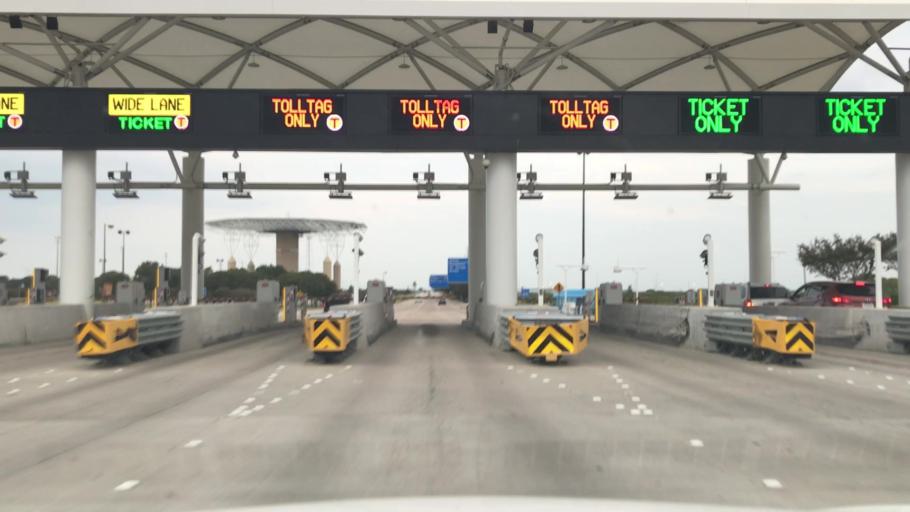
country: US
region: Texas
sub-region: Tarrant County
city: Euless
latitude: 32.8661
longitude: -97.0399
